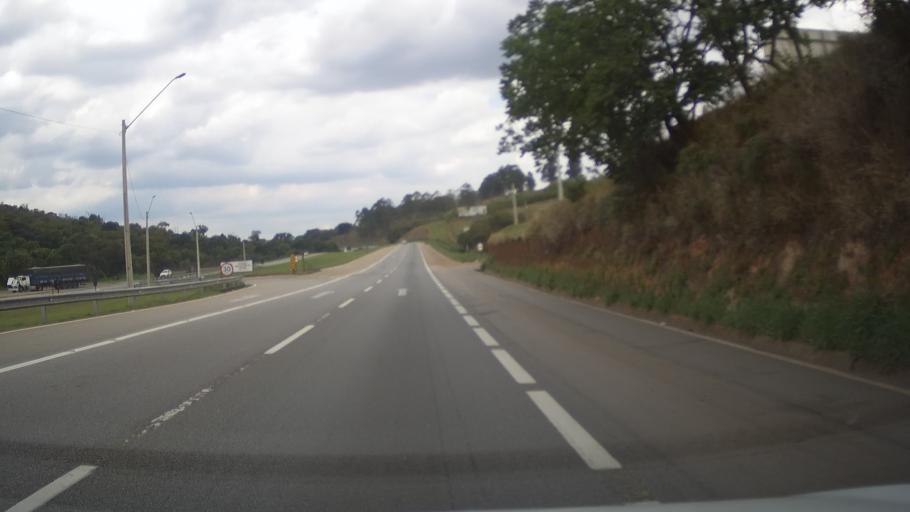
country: BR
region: Minas Gerais
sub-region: Tres Coracoes
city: Tres Coracoes
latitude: -21.5275
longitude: -45.2283
